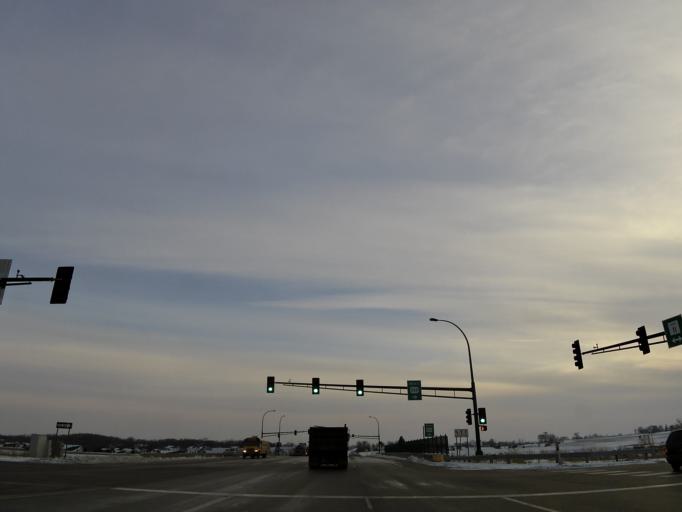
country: US
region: Minnesota
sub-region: Carver County
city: Carver
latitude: 44.7781
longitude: -93.6426
